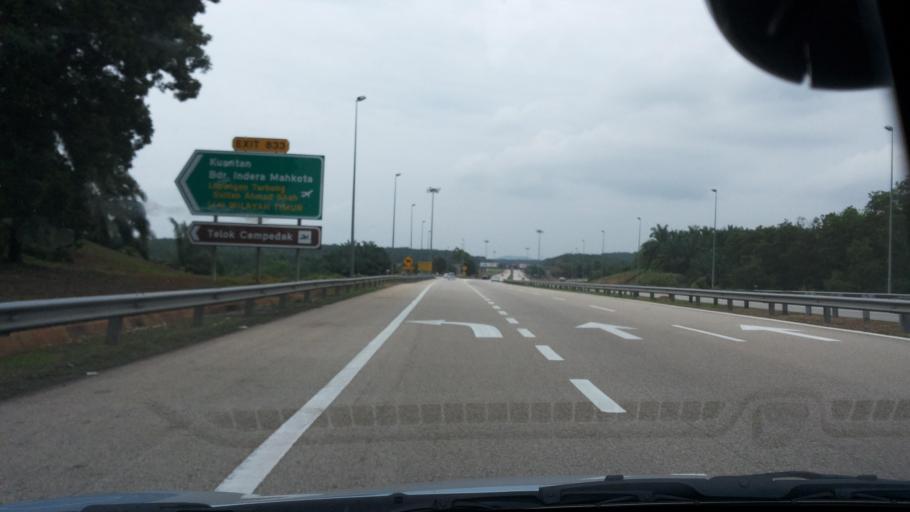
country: MY
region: Pahang
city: Kuantan
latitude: 3.8699
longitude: 103.2369
